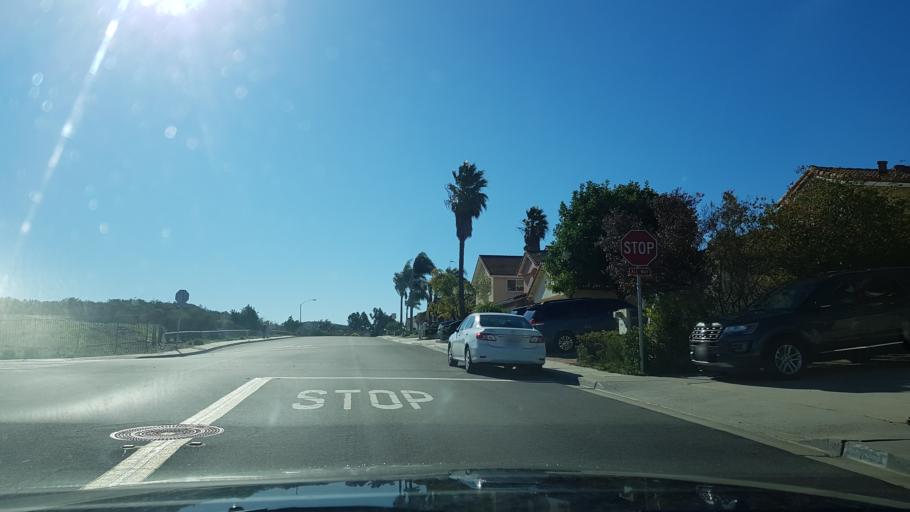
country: US
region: California
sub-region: San Diego County
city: Fairbanks Ranch
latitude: 32.9515
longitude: -117.1203
